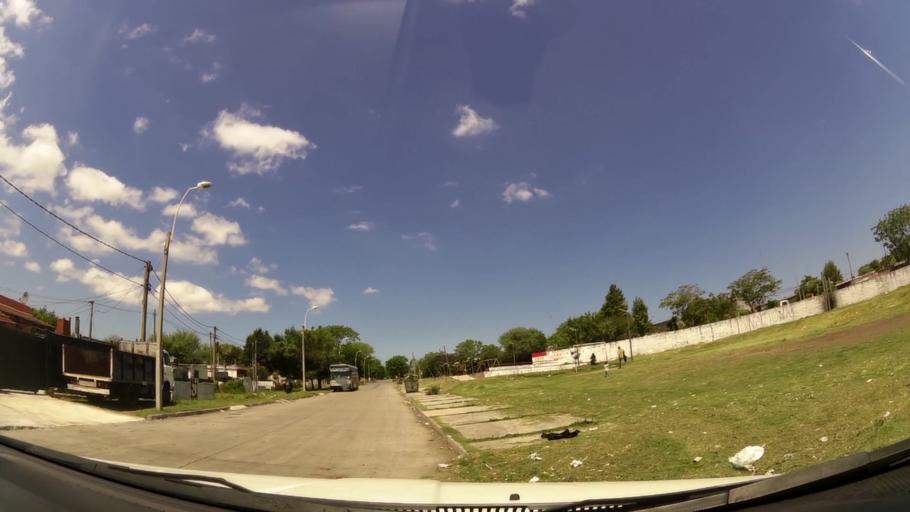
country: UY
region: Montevideo
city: Montevideo
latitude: -34.8526
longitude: -56.2358
